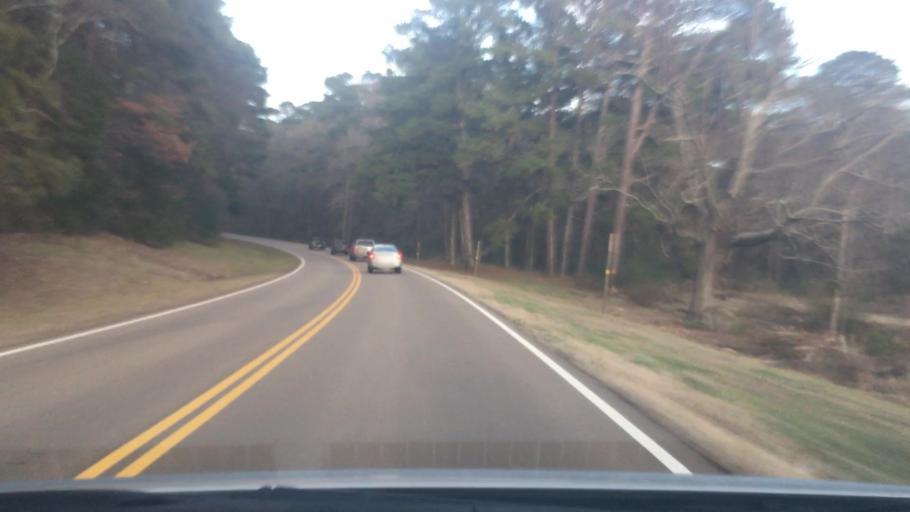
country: US
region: Mississippi
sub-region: Madison County
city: Canton
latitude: 32.5169
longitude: -89.9836
